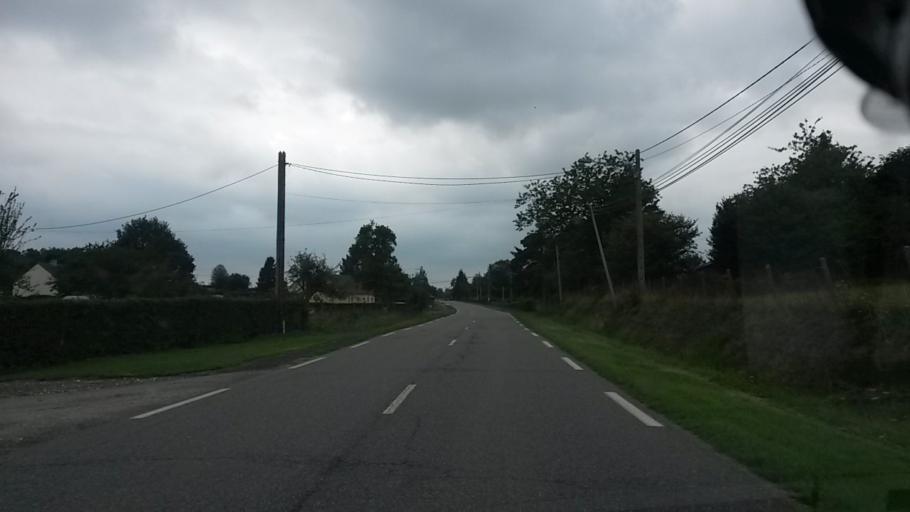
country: FR
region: Haute-Normandie
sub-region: Departement de la Seine-Maritime
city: Gaillefontaine
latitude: 49.7024
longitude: 1.6523
